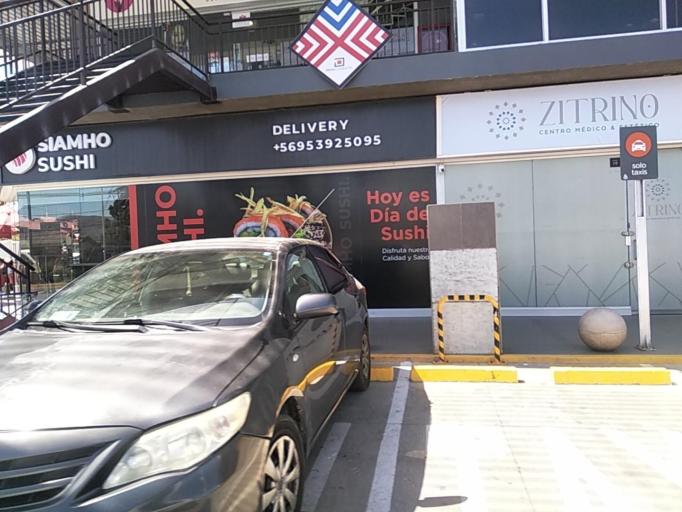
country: CL
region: Atacama
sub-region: Provincia de Copiapo
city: Copiapo
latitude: -27.3978
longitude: -70.2945
